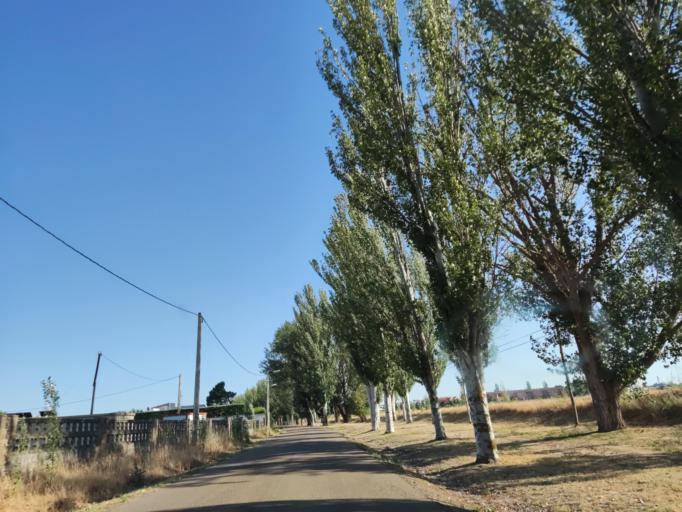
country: ES
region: Castille and Leon
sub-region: Provincia de Zamora
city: Villaralbo
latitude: 41.4996
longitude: -5.6860
